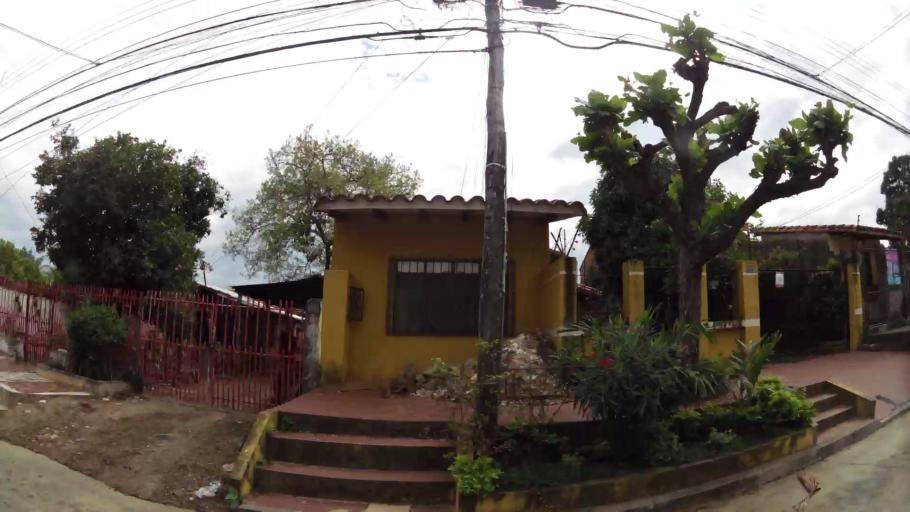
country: BO
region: Santa Cruz
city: Santa Cruz de la Sierra
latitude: -17.7493
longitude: -63.1924
